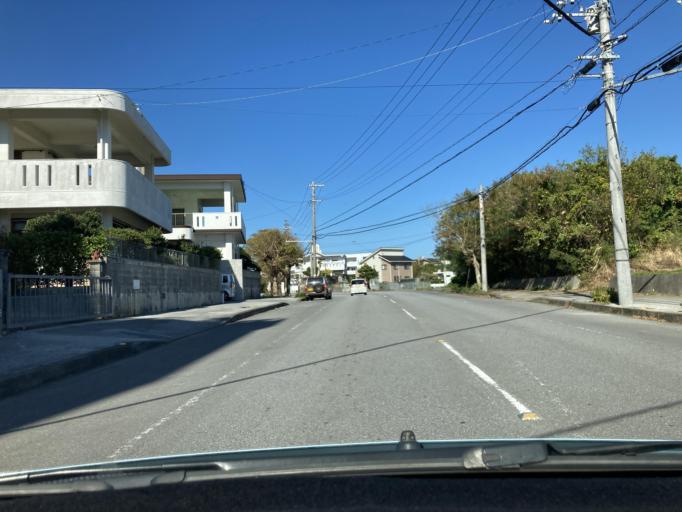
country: JP
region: Okinawa
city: Gushikawa
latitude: 26.3832
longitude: 127.8693
